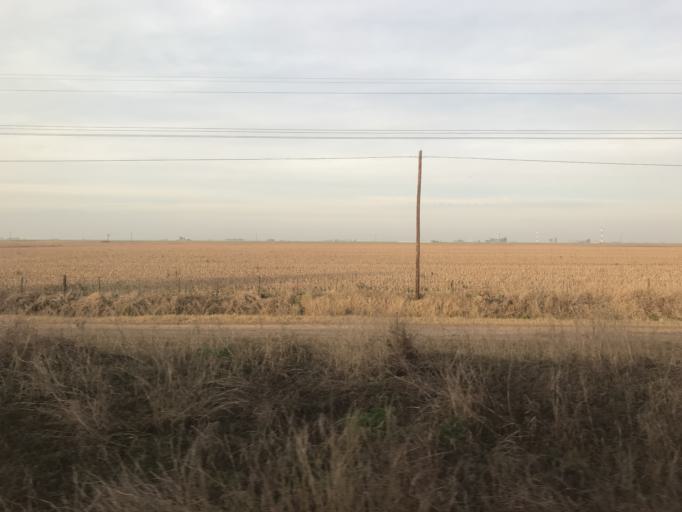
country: AR
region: Cordoba
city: Marcos Juarez
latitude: -32.6852
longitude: -62.1836
